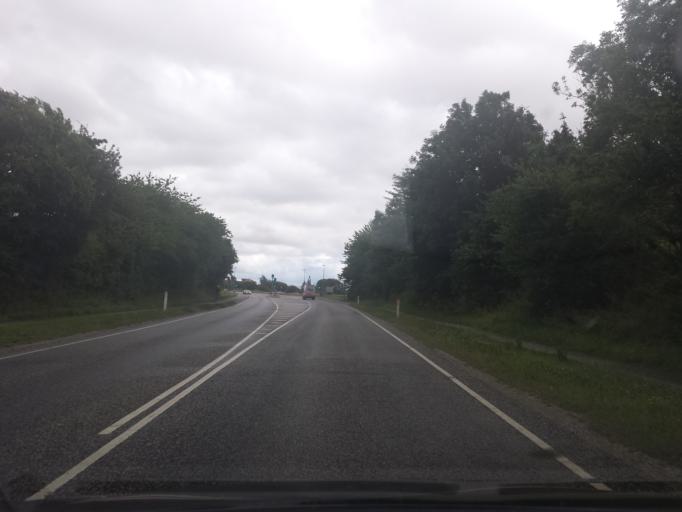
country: DK
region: South Denmark
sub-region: Sonderborg Kommune
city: Guderup
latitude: 54.9890
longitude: 9.8605
